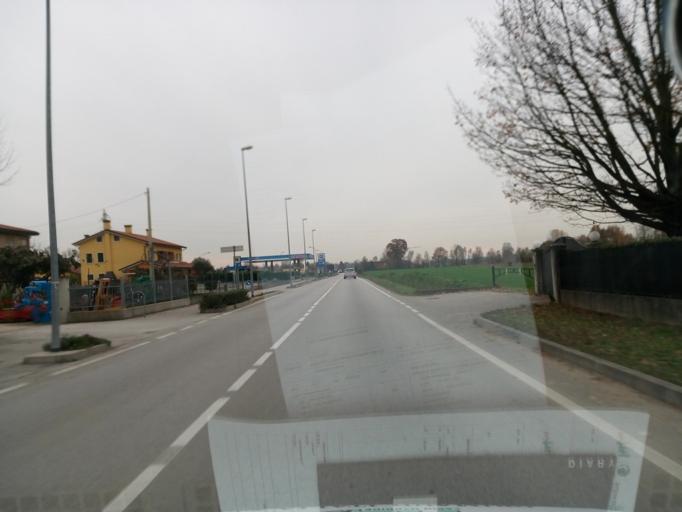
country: IT
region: Veneto
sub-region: Provincia di Padova
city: Massanzago-Ca' Baglioni-San Dono
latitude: 45.5735
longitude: 12.0033
